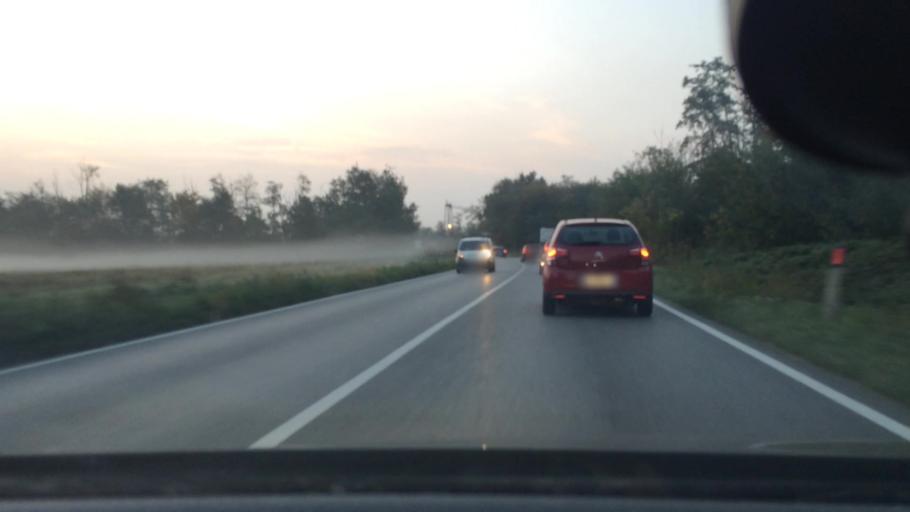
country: IT
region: Lombardy
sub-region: Citta metropolitana di Milano
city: Vanzago
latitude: 45.5318
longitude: 8.9696
